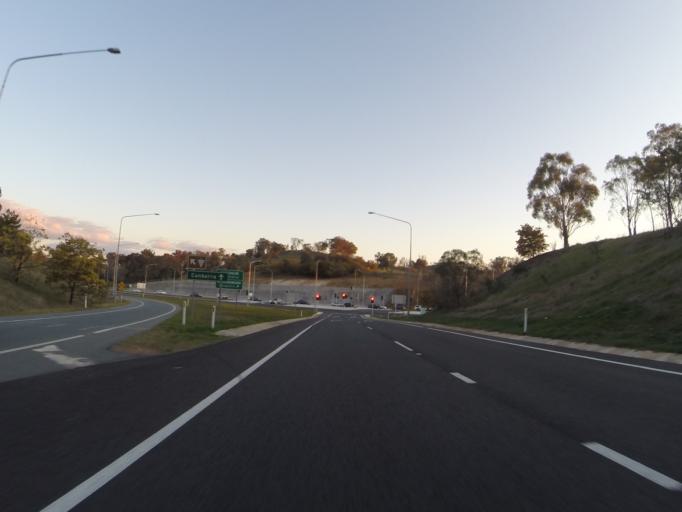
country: AU
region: Australian Capital Territory
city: Kaleen
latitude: -35.2134
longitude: 149.1891
